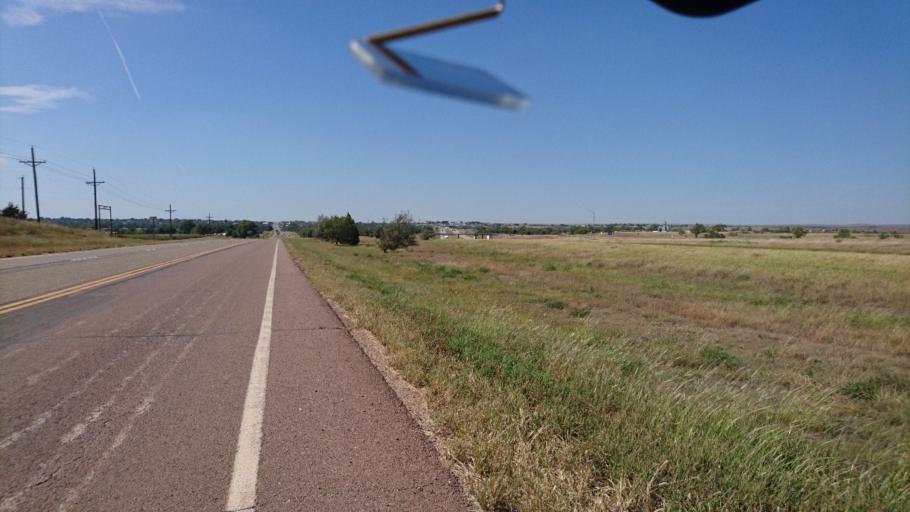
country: US
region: Texas
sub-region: Wheeler County
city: Shamrock
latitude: 35.2266
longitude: -100.2202
